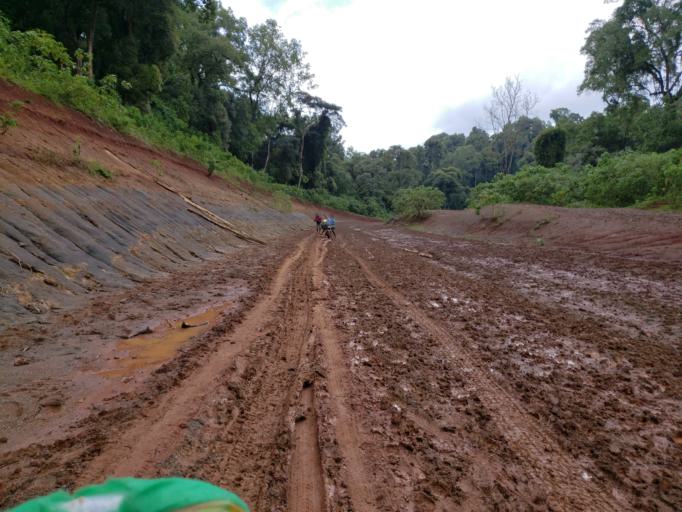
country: ET
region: Oromiya
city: Dodola
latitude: 6.4677
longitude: 39.5309
